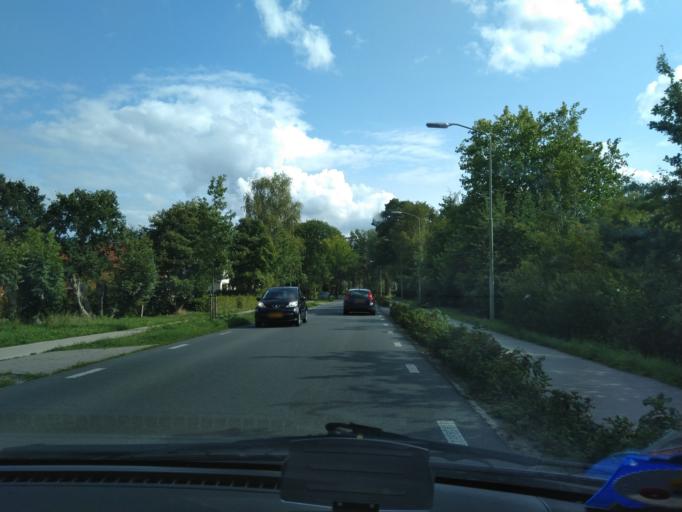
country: NL
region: Groningen
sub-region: Gemeente Groningen
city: Groningen
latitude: 53.1716
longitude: 6.5481
